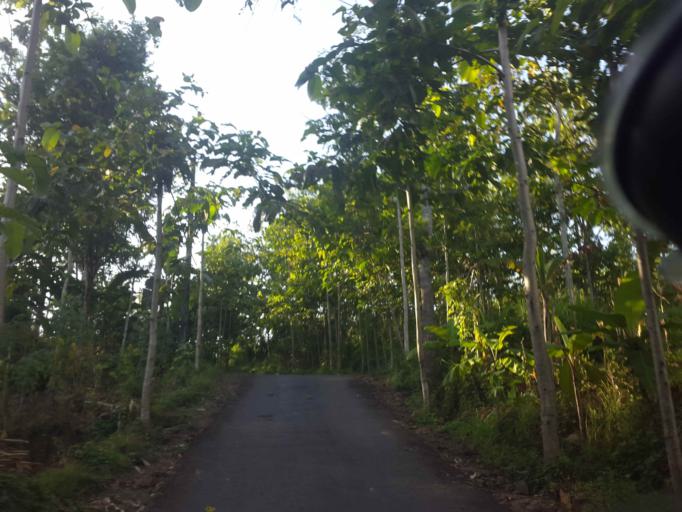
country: ID
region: Central Java
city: Jatiroto
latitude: -7.7909
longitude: 111.1065
